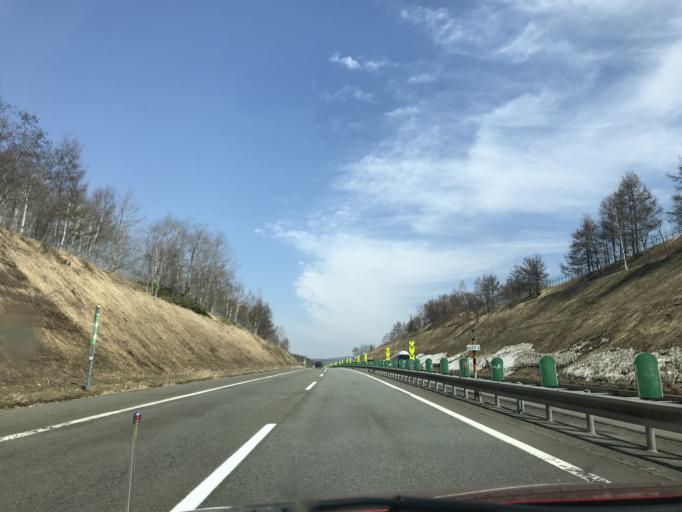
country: JP
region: Hokkaido
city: Iwamizawa
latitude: 43.2054
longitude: 141.8147
